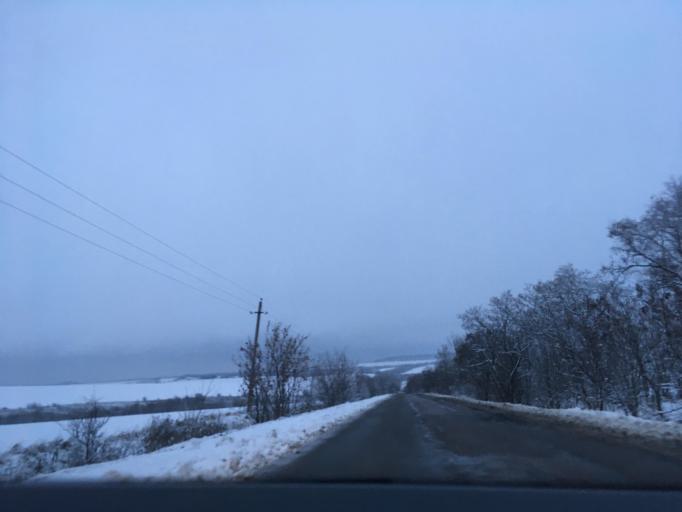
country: RU
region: Voronezj
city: Verkhniy Mamon
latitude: 50.0497
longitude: 40.2433
